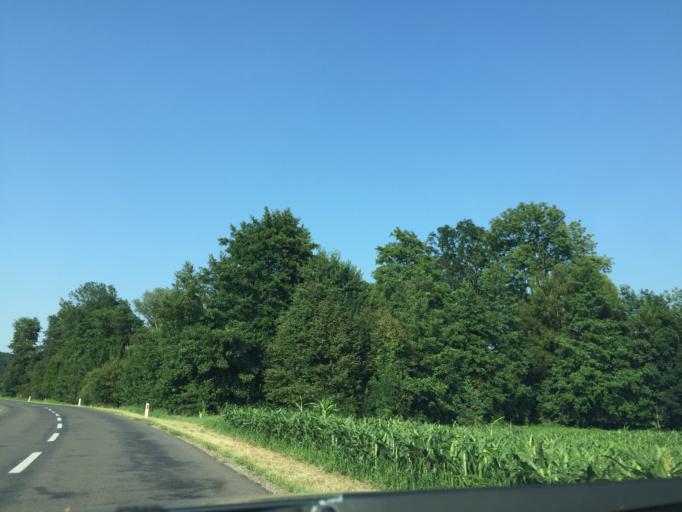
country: AT
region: Styria
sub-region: Politischer Bezirk Suedoststeiermark
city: Deutsch Goritz
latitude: 46.7550
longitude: 15.8380
